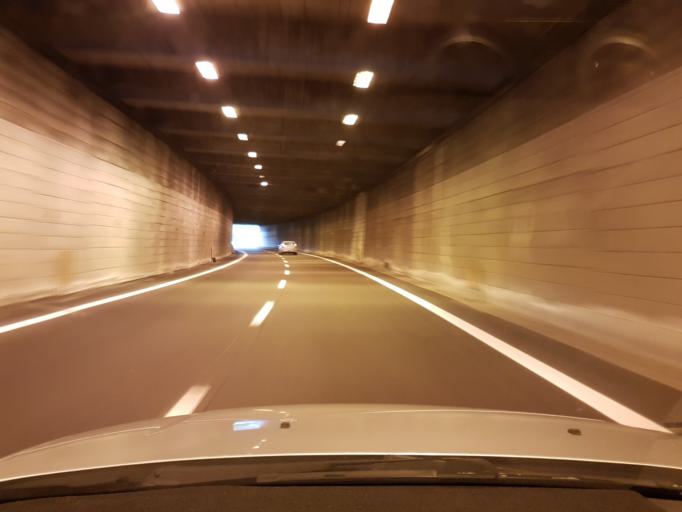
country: IT
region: Sardinia
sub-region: Provincia di Nuoro
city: Nuoro
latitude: 40.3480
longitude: 9.3332
